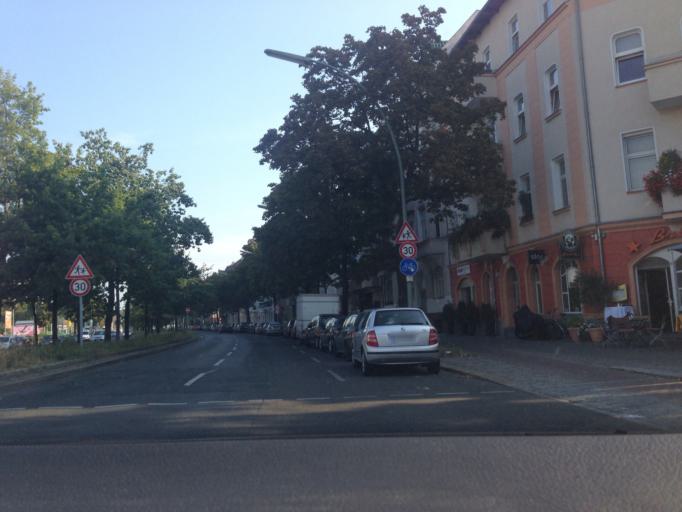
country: DE
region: Berlin
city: Wilhelmstadt
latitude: 52.5250
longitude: 13.1934
